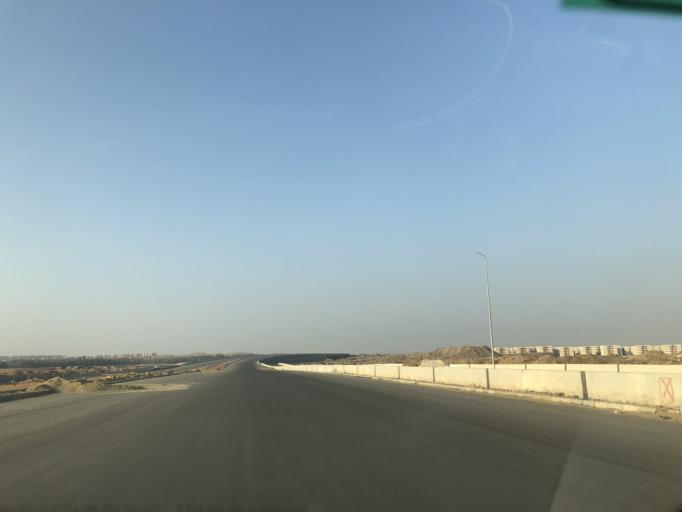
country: EG
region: Al Jizah
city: Madinat Sittah Uktubar
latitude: 29.9091
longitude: 31.0163
